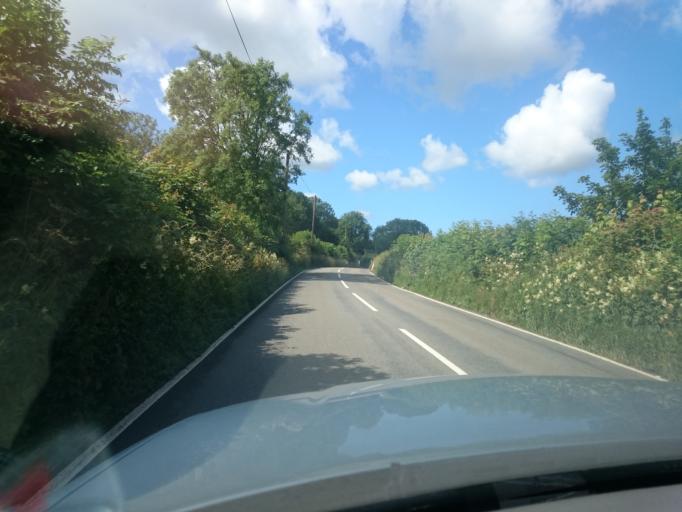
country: GB
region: Wales
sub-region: Pembrokeshire
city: Haverfordwest
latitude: 51.7865
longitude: -4.9877
